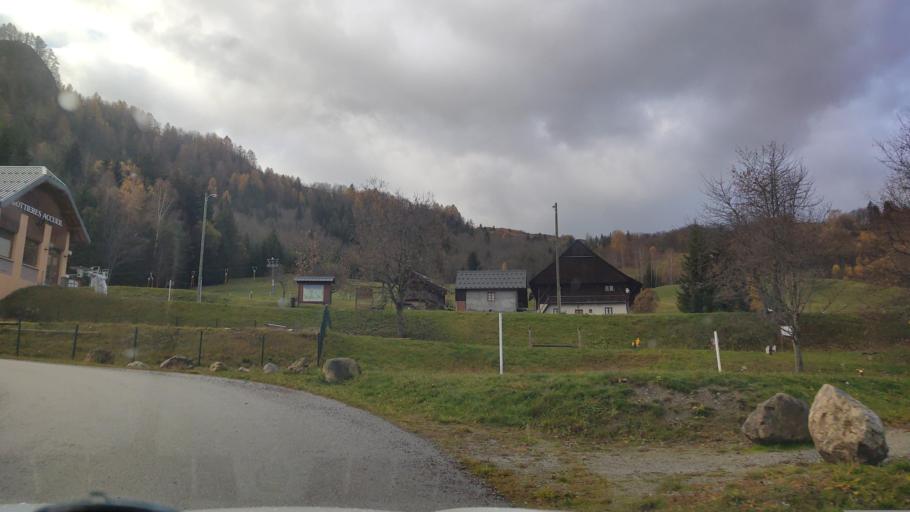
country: FR
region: Rhone-Alpes
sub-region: Departement de la Savoie
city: Saint-Jean-de-Maurienne
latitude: 45.2657
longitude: 6.2980
